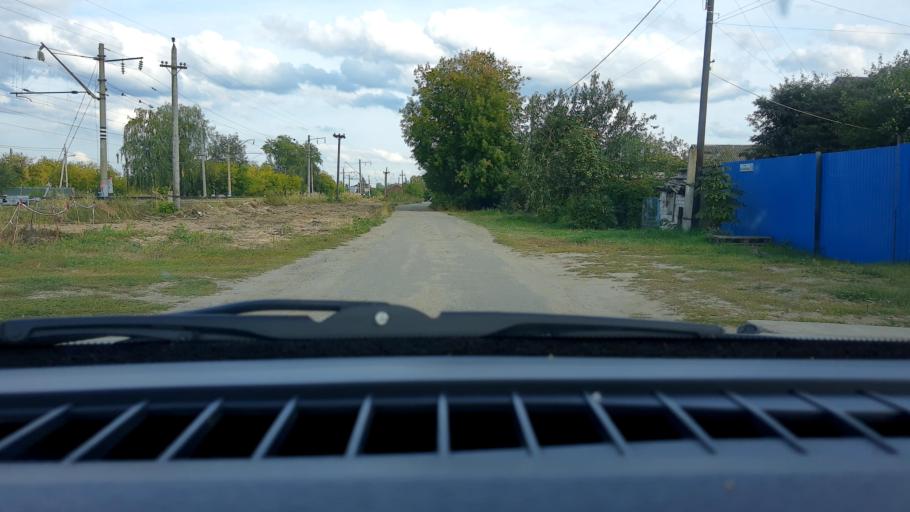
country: RU
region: Nizjnij Novgorod
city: Gorbatovka
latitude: 56.3725
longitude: 43.8156
